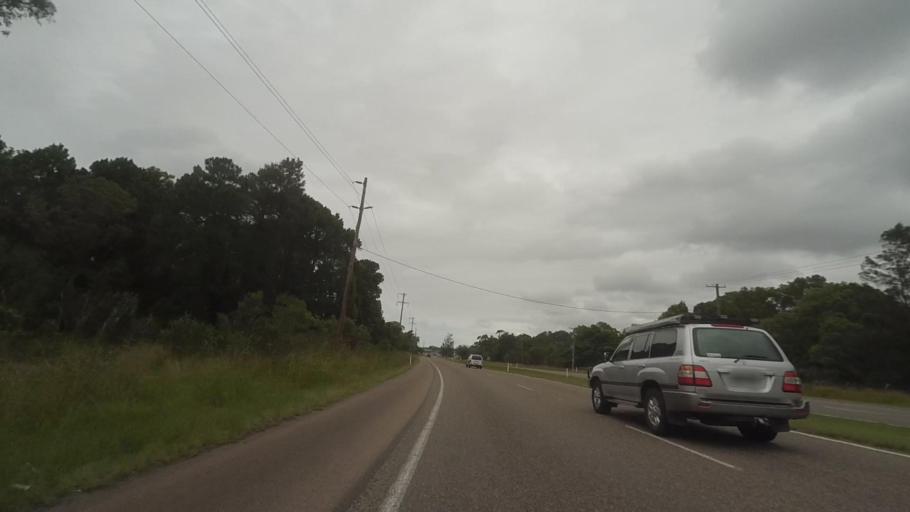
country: AU
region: New South Wales
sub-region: Wyong Shire
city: Buff Point
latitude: -33.1915
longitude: 151.5277
